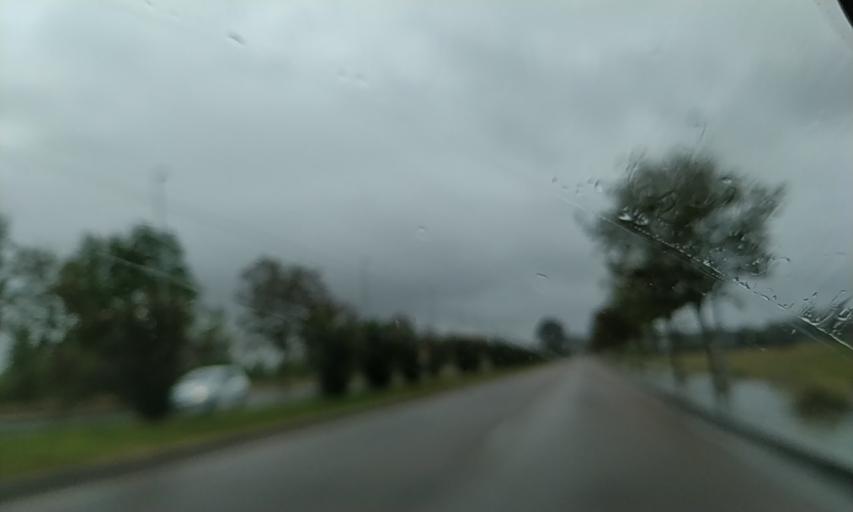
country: ES
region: Extremadura
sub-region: Provincia de Badajoz
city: Badajoz
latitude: 38.8999
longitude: -6.9686
